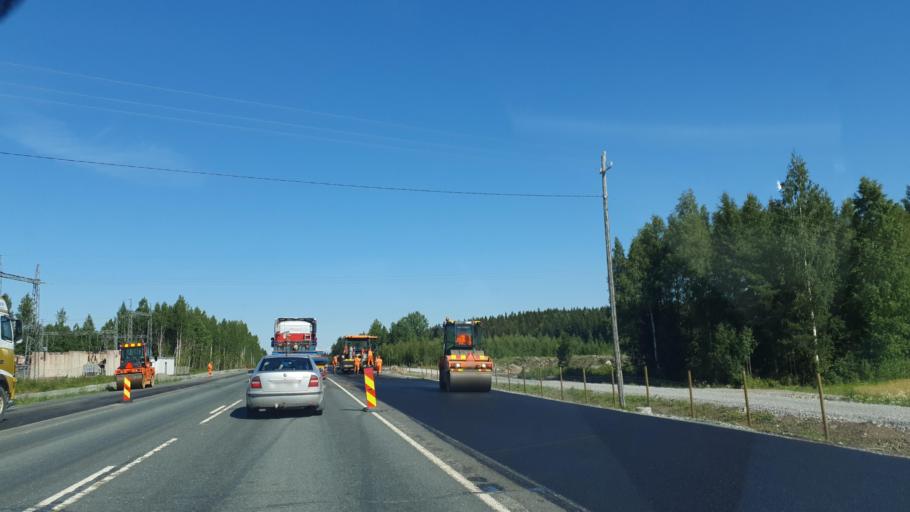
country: FI
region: Northern Savo
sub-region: Ylae-Savo
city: Lapinlahti
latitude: 63.2890
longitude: 27.4546
